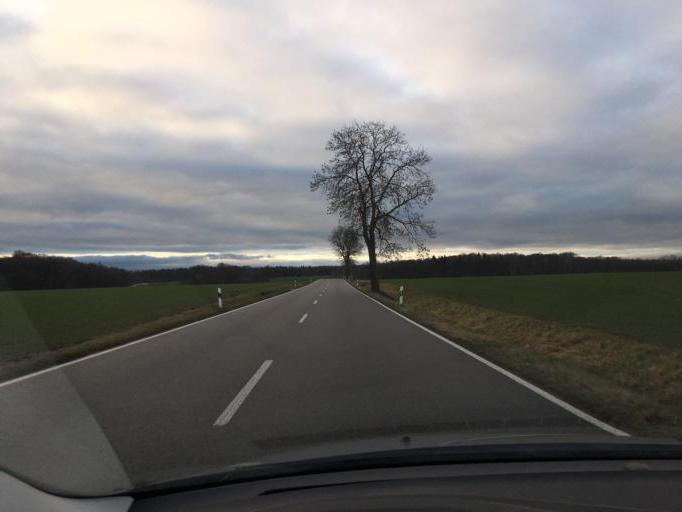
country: DE
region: Saxony
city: Frohburg
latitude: 51.0075
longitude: 12.5600
